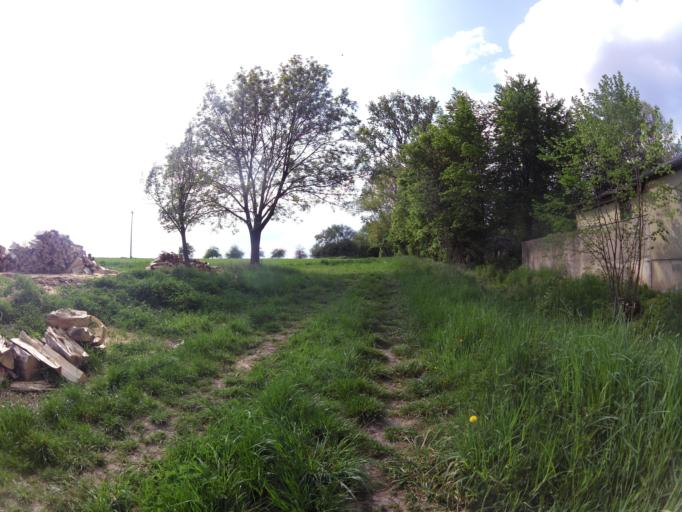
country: DE
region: Bavaria
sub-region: Regierungsbezirk Unterfranken
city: Giebelstadt
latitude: 49.6327
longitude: 9.9427
